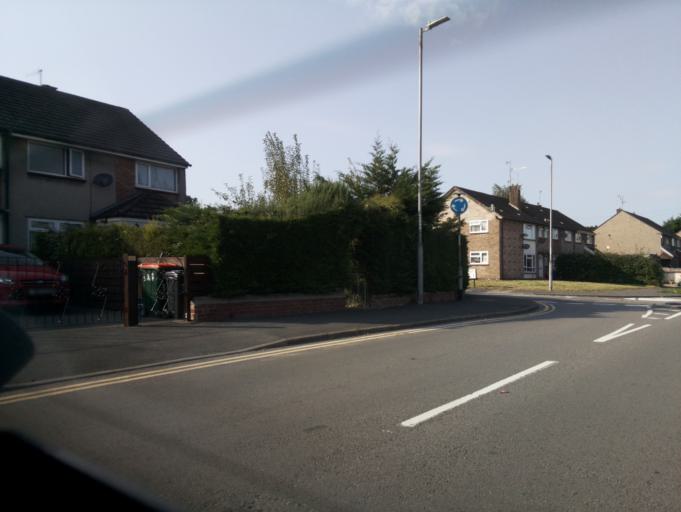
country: GB
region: Wales
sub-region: Newport
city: Newport
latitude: 51.6095
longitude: -3.0362
